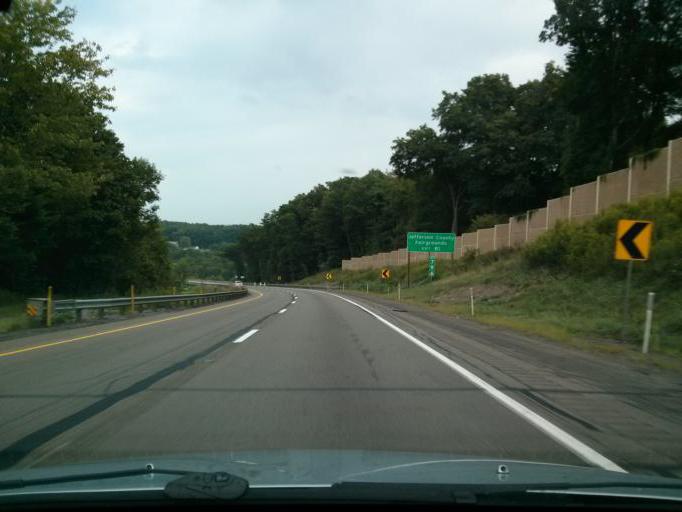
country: US
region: Pennsylvania
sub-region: Jefferson County
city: Brookville
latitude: 41.1685
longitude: -79.0789
